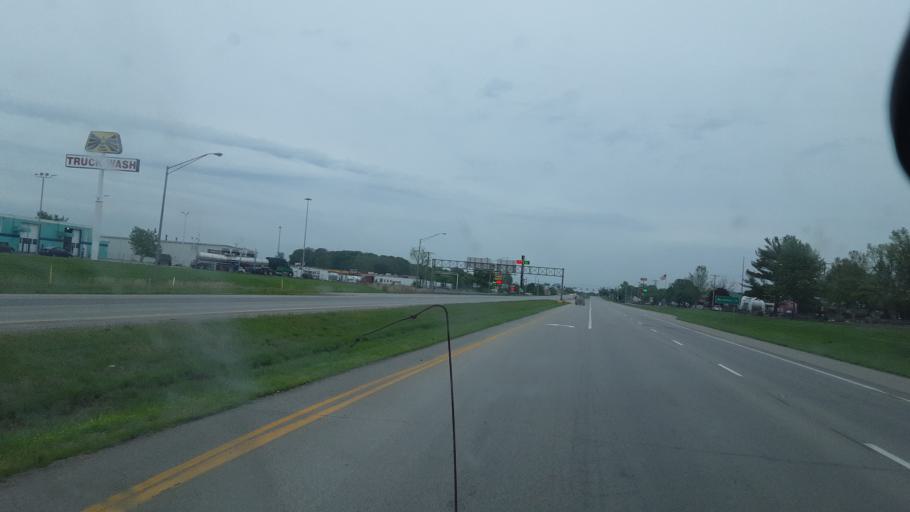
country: US
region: Indiana
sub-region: Gibson County
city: Haubstadt
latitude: 38.1699
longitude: -87.5504
